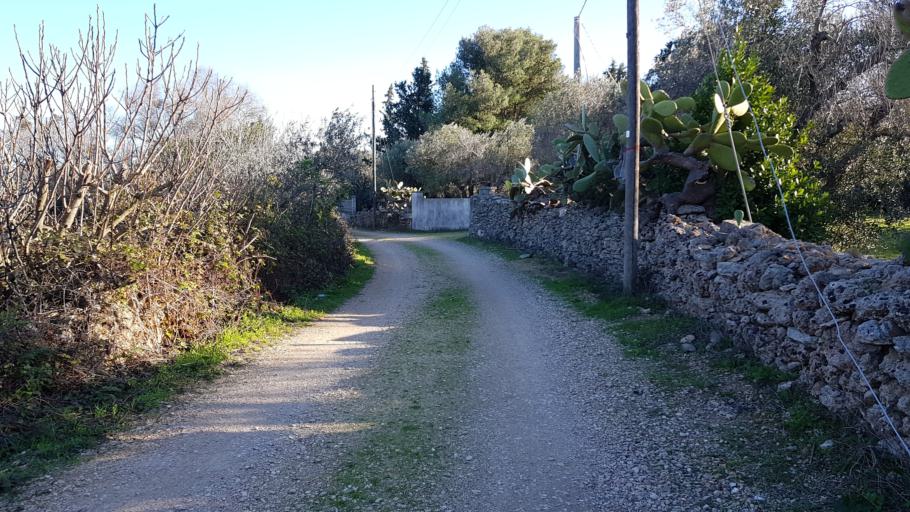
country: IT
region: Apulia
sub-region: Provincia di Lecce
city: Nardo
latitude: 40.1579
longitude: 17.9725
